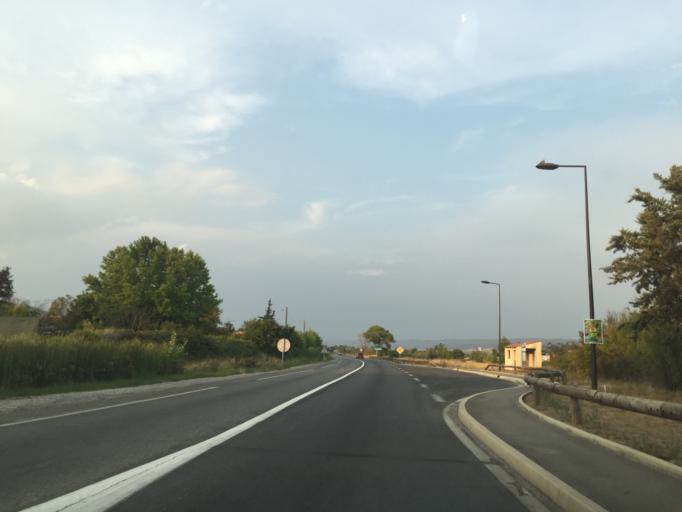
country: FR
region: Provence-Alpes-Cote d'Azur
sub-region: Departement des Alpes-de-Haute-Provence
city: Villeneuve
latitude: 43.8887
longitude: 5.8702
